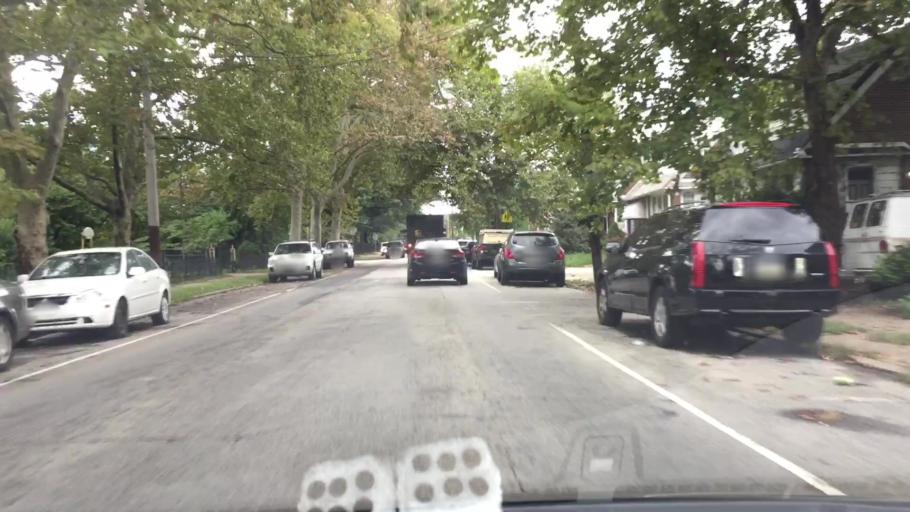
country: US
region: New Jersey
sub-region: Burlington County
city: Palmyra
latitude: 40.0180
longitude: -75.0655
